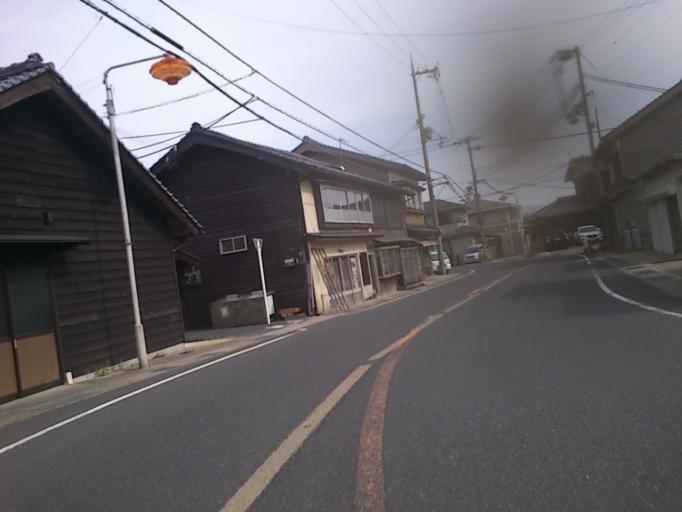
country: JP
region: Kyoto
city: Miyazu
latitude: 35.6895
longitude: 135.0178
